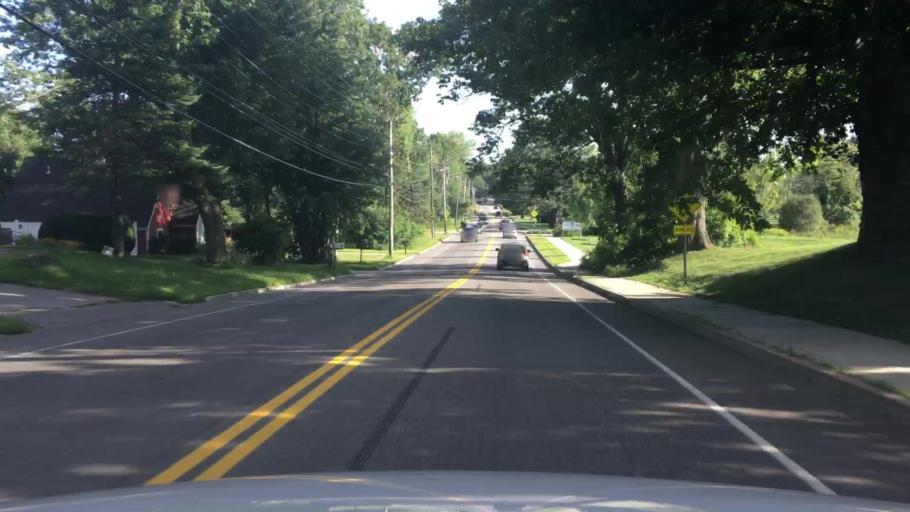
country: US
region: Maine
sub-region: Cumberland County
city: Scarborough
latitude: 43.5862
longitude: -70.3336
